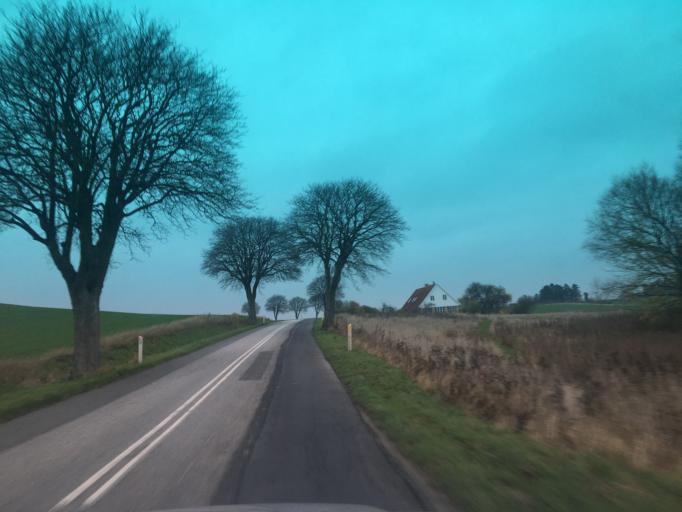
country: DK
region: Zealand
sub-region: Slagelse Kommune
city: Skaelskor
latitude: 55.2559
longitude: 11.4190
